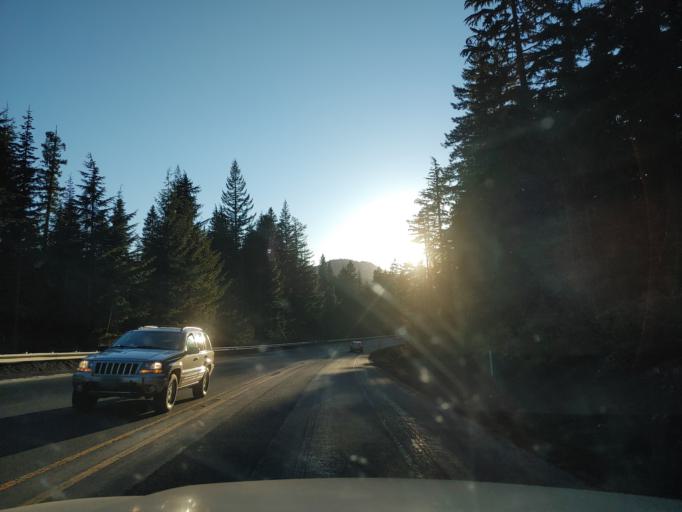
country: US
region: Oregon
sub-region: Lane County
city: Oakridge
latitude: 43.6108
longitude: -122.1206
